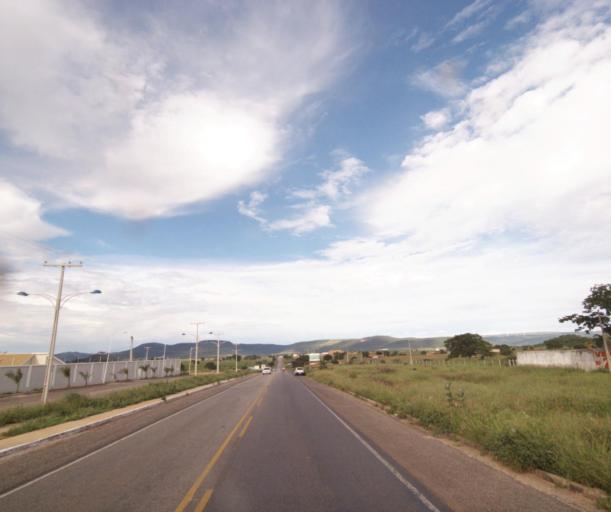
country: BR
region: Bahia
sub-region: Guanambi
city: Guanambi
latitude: -14.1984
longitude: -42.7525
